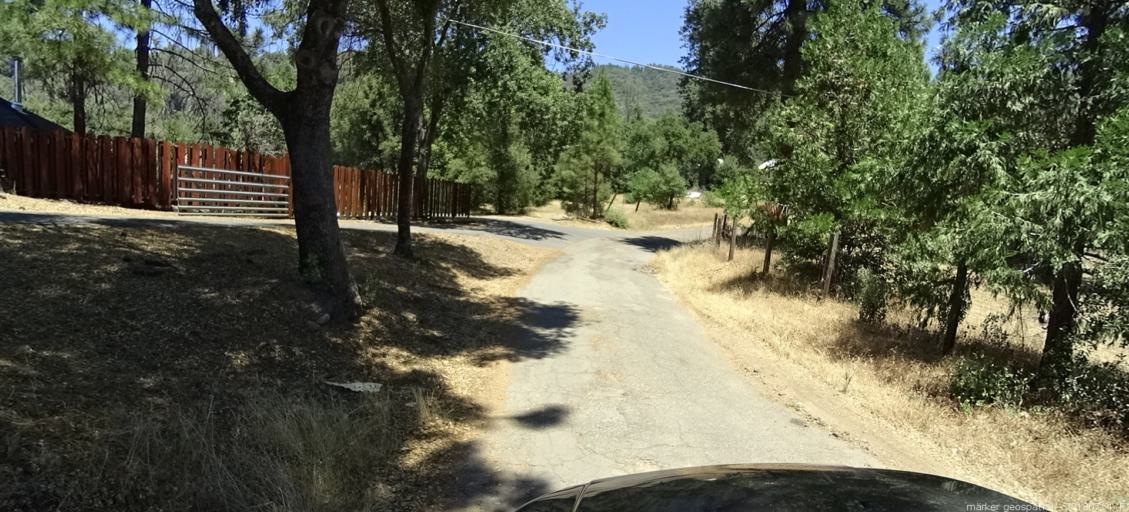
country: US
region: California
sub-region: Madera County
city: Ahwahnee
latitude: 37.4187
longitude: -119.7123
